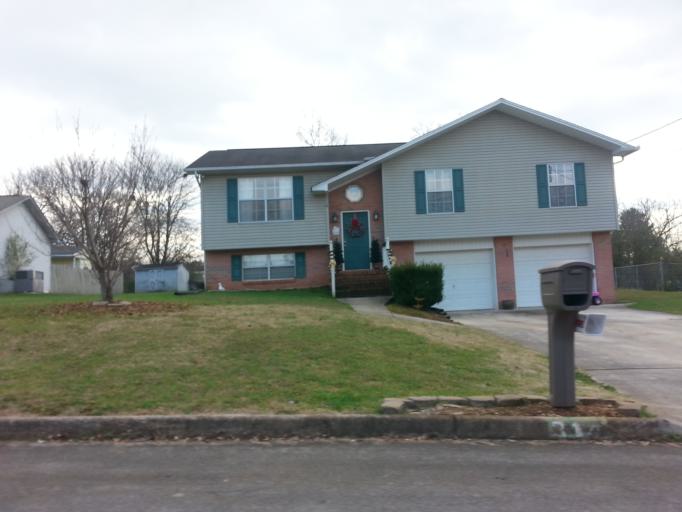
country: US
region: Tennessee
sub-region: Blount County
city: Eagleton Village
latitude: 35.7965
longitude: -83.9378
